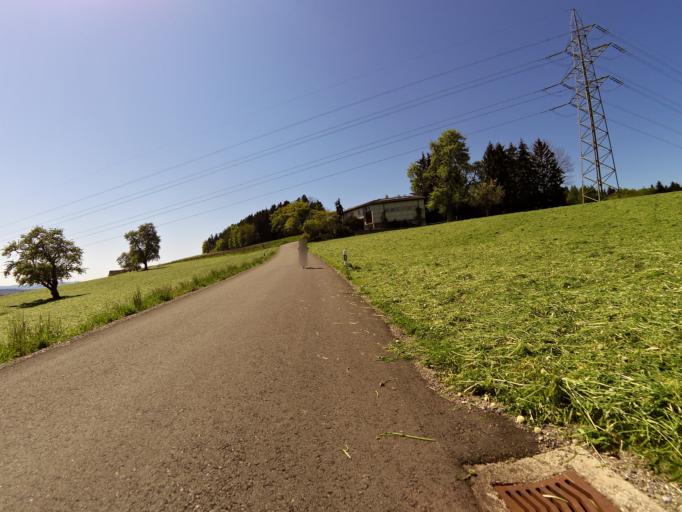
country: CH
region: Thurgau
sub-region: Weinfelden District
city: Berg
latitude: 47.5817
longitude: 9.1596
